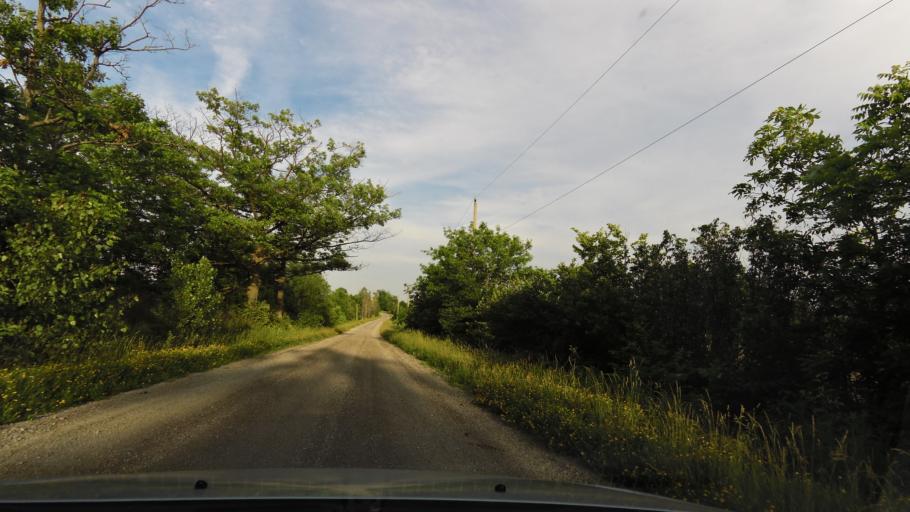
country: CA
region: Ontario
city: Ancaster
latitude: 43.0709
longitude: -79.9692
